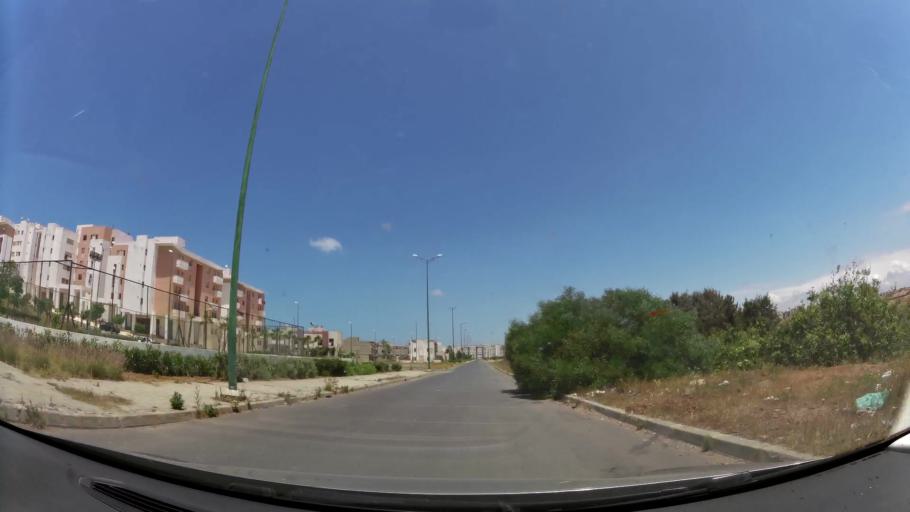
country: MA
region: Gharb-Chrarda-Beni Hssen
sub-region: Kenitra Province
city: Kenitra
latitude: 34.2495
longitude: -6.6496
